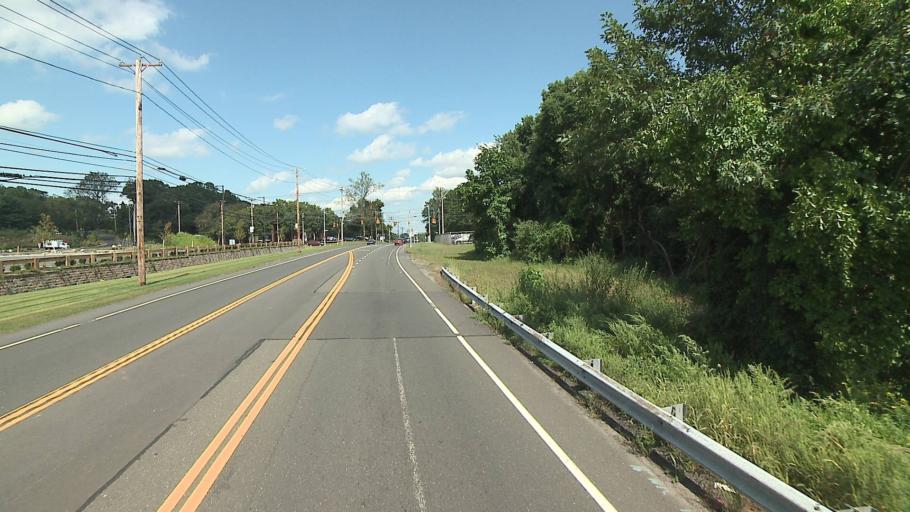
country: US
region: Connecticut
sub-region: Fairfield County
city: Shelton
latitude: 41.2945
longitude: -73.1096
